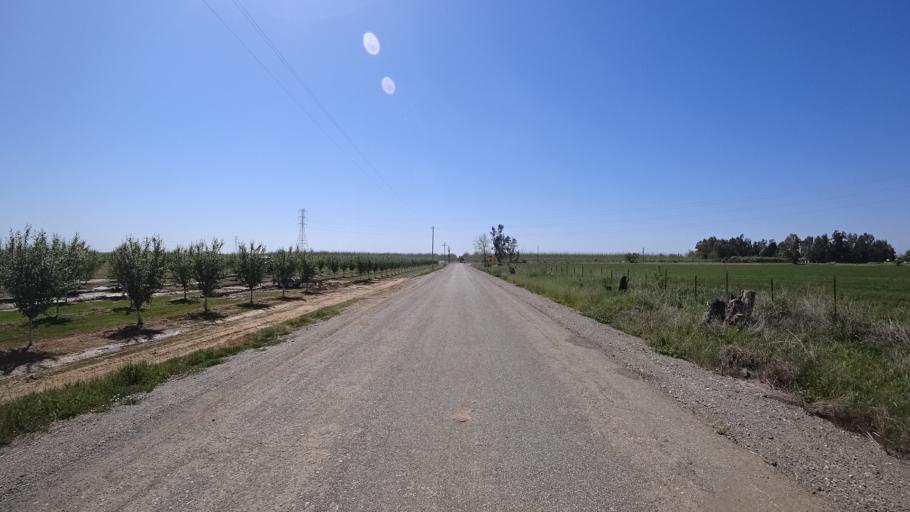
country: US
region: California
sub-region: Glenn County
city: Orland
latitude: 39.7891
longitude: -122.1504
